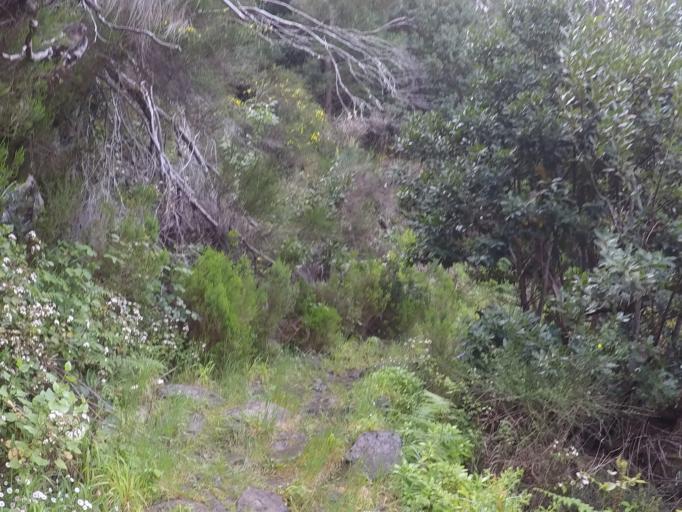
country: PT
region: Madeira
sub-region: Camara de Lobos
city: Curral das Freiras
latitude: 32.7474
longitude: -17.0051
